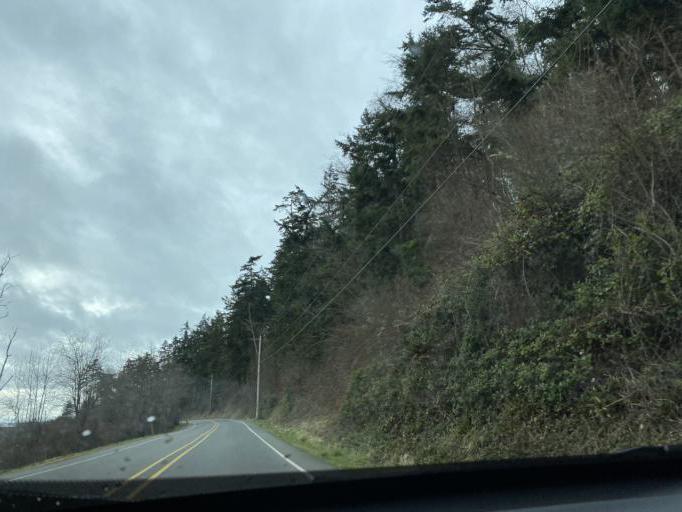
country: US
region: Washington
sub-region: Island County
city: Freeland
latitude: 47.9855
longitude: -122.5135
